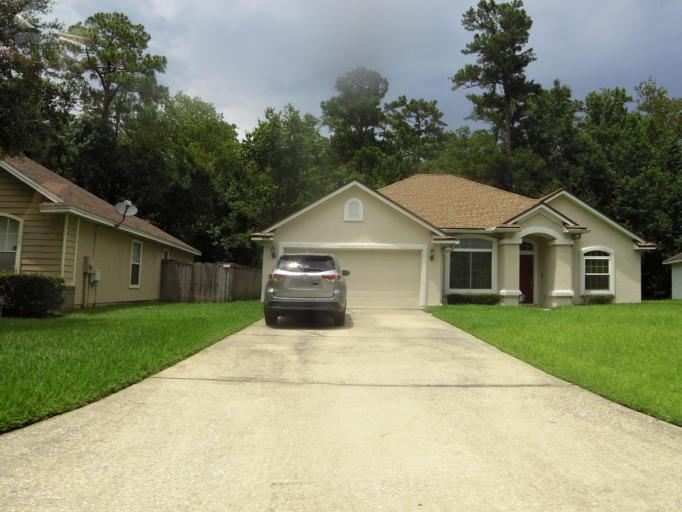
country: US
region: Florida
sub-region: Nassau County
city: Nassau Village-Ratliff
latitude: 30.4269
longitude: -81.7274
